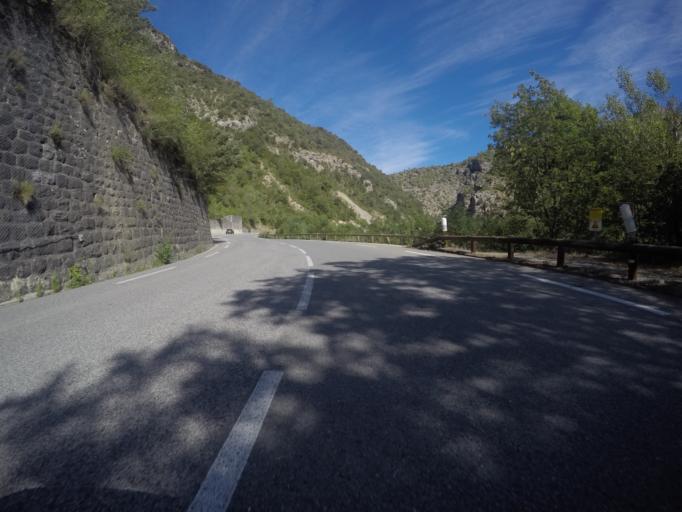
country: FR
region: Provence-Alpes-Cote d'Azur
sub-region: Departement des Alpes-Maritimes
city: Gilette
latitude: 43.9335
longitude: 7.1733
